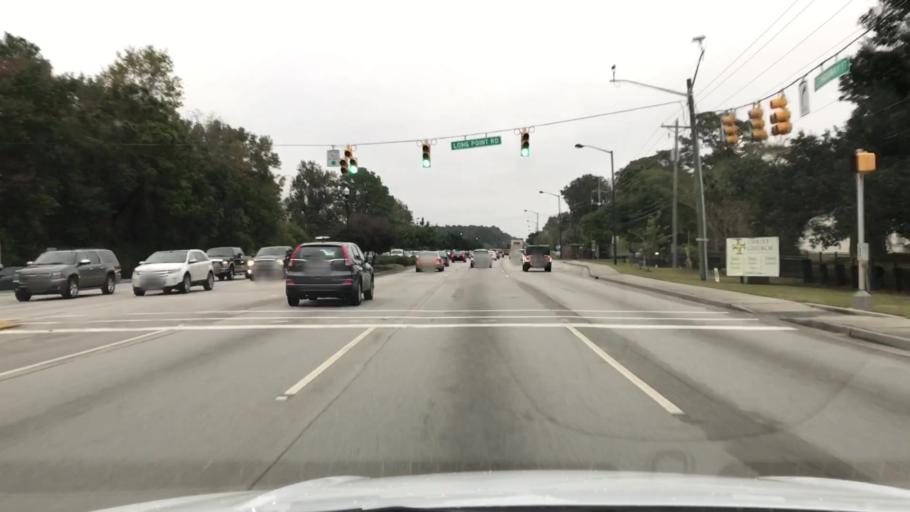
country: US
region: South Carolina
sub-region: Charleston County
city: Isle of Palms
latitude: 32.8443
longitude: -79.8142
